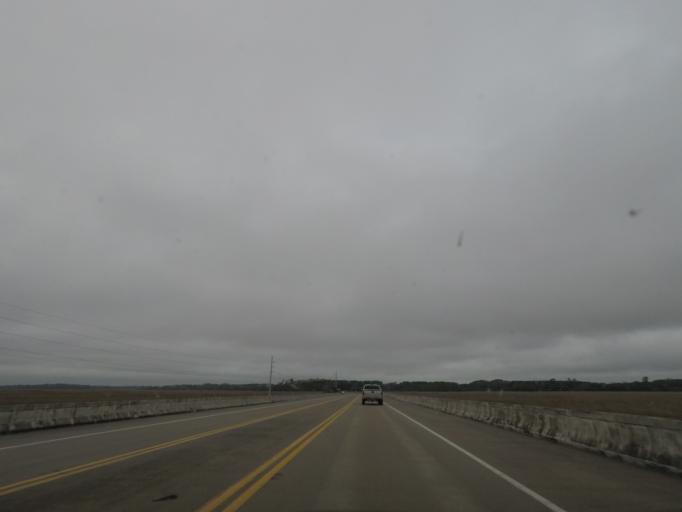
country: US
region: South Carolina
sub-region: Charleston County
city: Meggett
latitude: 32.6449
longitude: -80.3423
